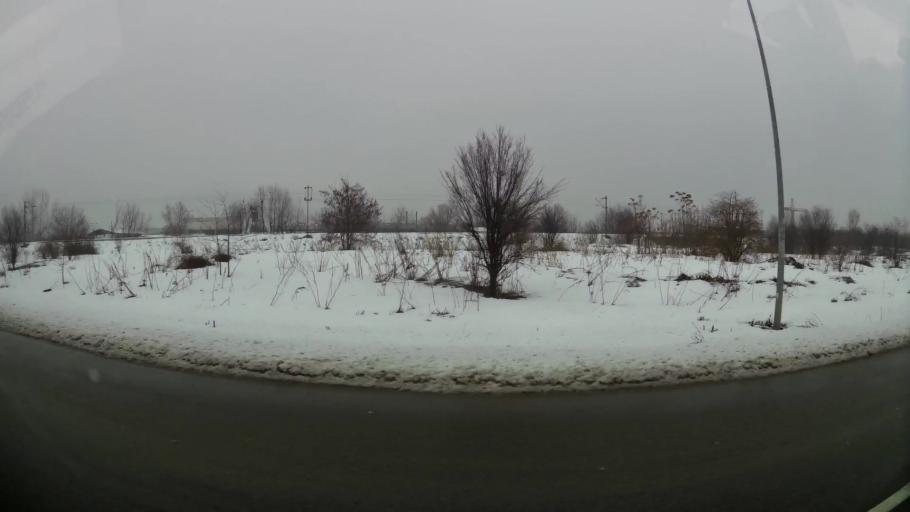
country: RS
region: Central Serbia
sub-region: Belgrade
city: Zemun
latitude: 44.8408
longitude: 20.3518
